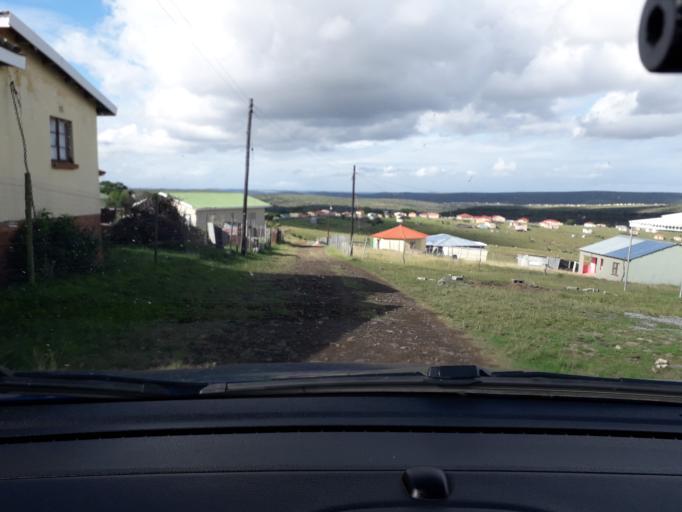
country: ZA
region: Eastern Cape
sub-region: Buffalo City Metropolitan Municipality
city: Bhisho
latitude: -33.1136
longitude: 27.4251
